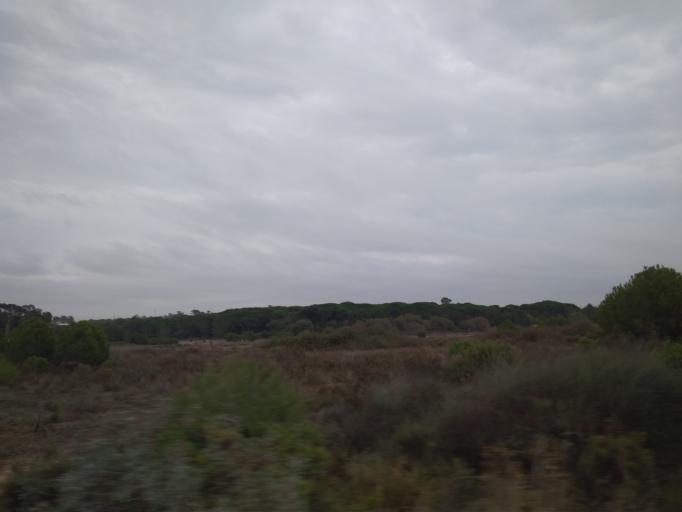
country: PT
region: Faro
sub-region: Faro
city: Faro
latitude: 37.0350
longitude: -7.9839
